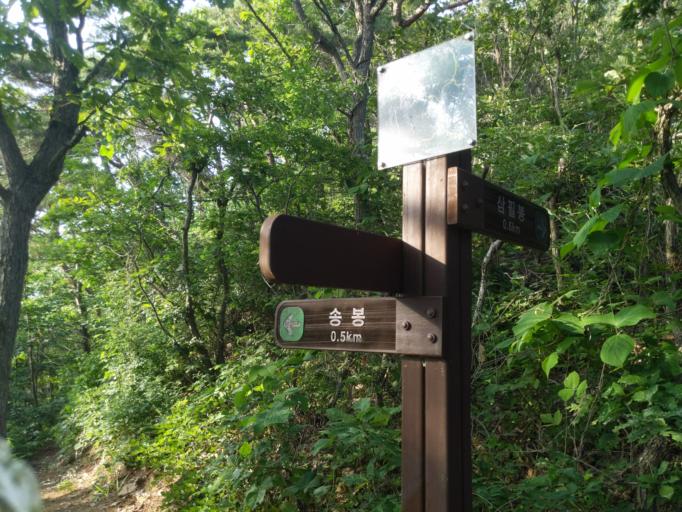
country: KR
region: Daegu
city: Hwawon
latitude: 35.7879
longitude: 128.5403
